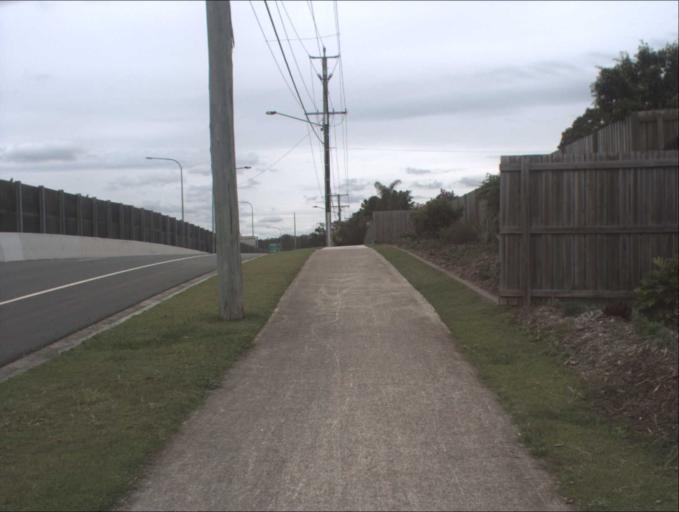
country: AU
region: Queensland
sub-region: Logan
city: Park Ridge South
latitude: -27.6849
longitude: 153.0313
